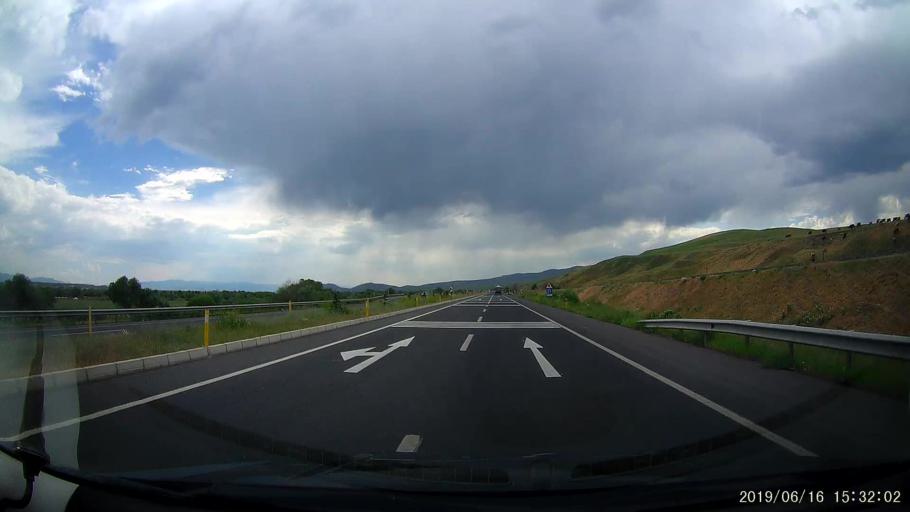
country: TR
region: Erzurum
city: Horasan
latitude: 40.0302
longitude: 42.0605
